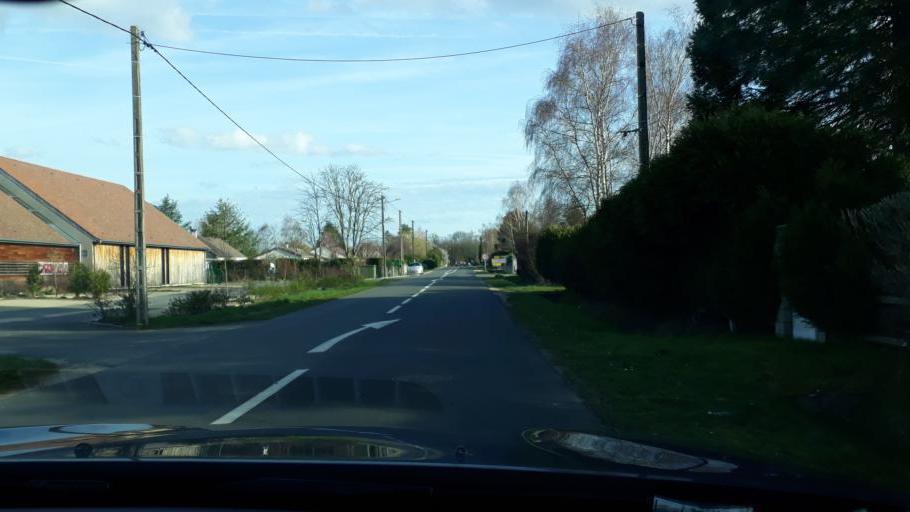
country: FR
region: Centre
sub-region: Departement du Loiret
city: Chilleurs-aux-Bois
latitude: 48.0571
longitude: 2.1748
